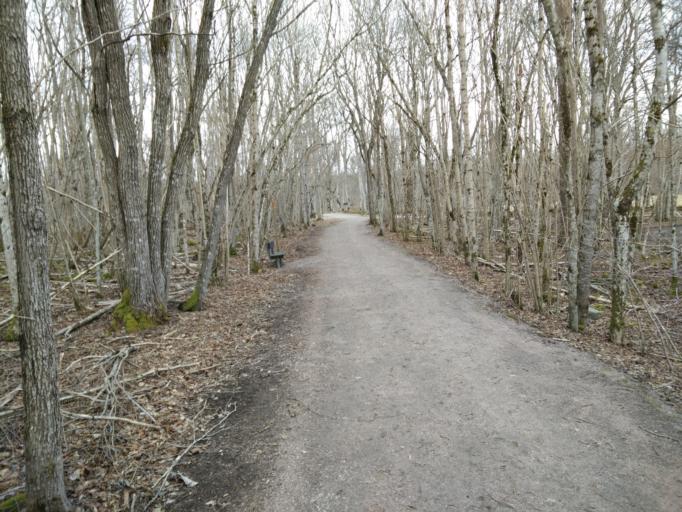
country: SE
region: OErebro
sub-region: Orebro Kommun
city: Garphyttan
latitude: 59.2784
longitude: 14.8837
